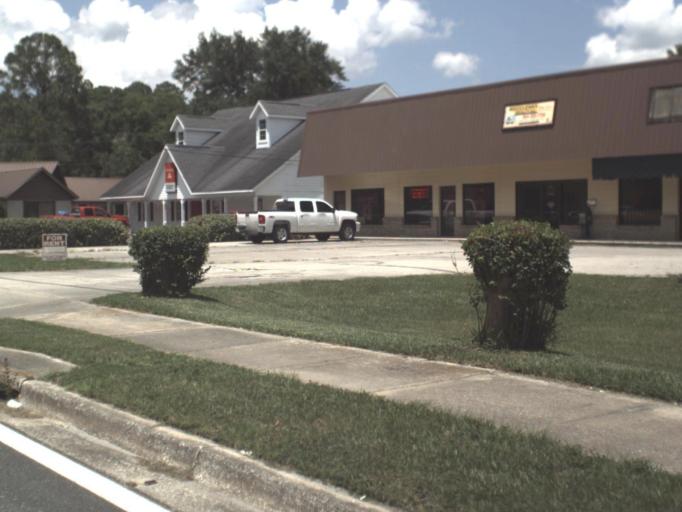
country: US
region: Florida
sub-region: Baker County
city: Macclenny
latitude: 30.2755
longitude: -82.1224
